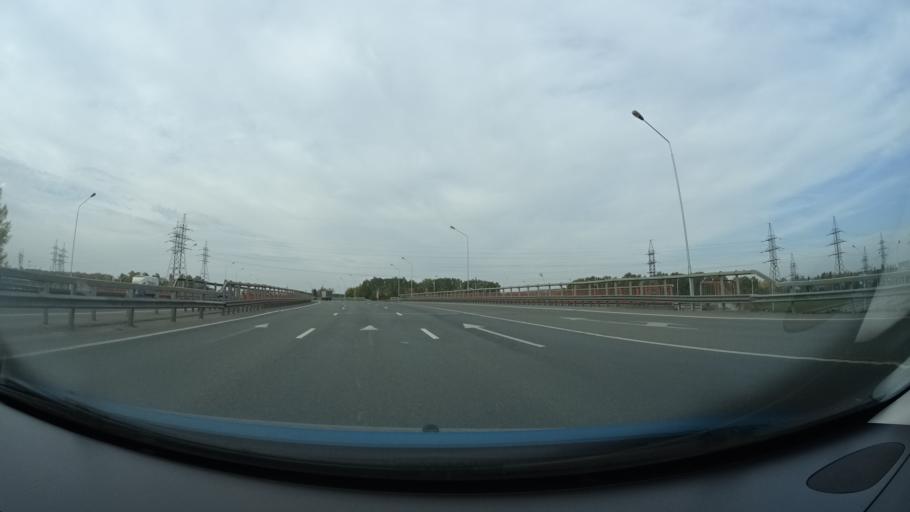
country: RU
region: Bashkortostan
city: Avdon
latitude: 54.6766
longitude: 55.8047
